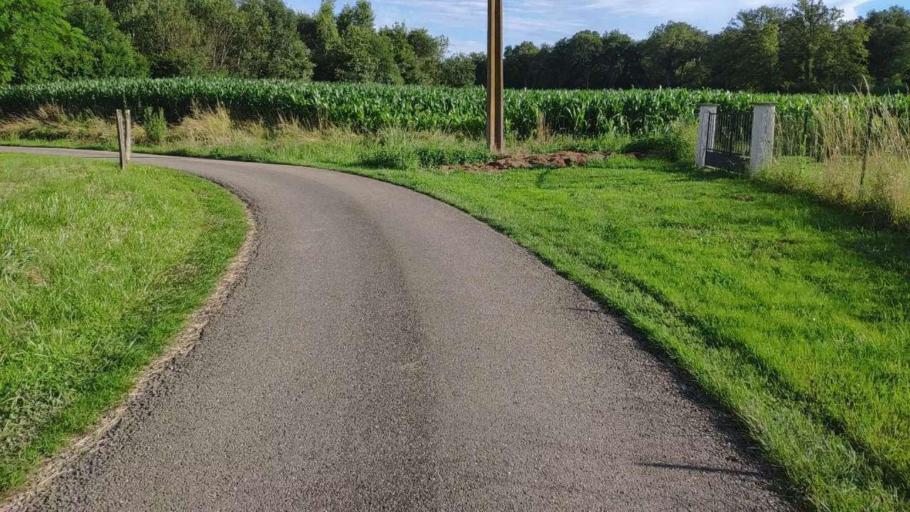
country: FR
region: Franche-Comte
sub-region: Departement du Jura
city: Bletterans
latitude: 46.7901
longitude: 5.4825
